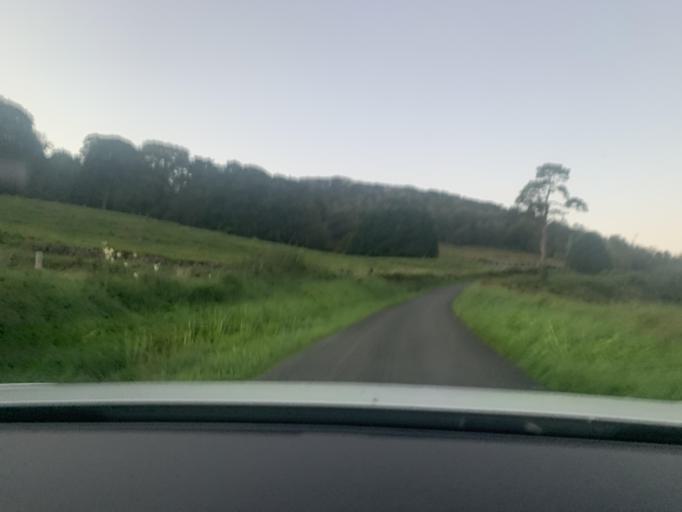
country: IE
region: Connaught
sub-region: County Leitrim
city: Manorhamilton
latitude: 54.2621
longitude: -8.2955
